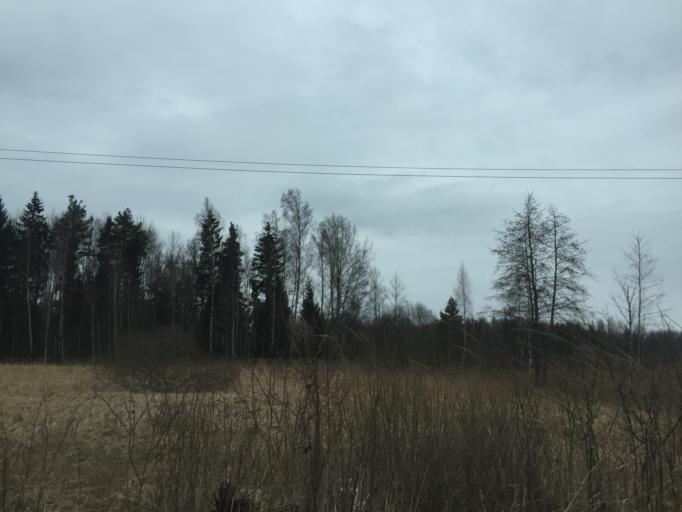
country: LV
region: Lielvarde
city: Lielvarde
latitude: 56.7575
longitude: 24.8284
